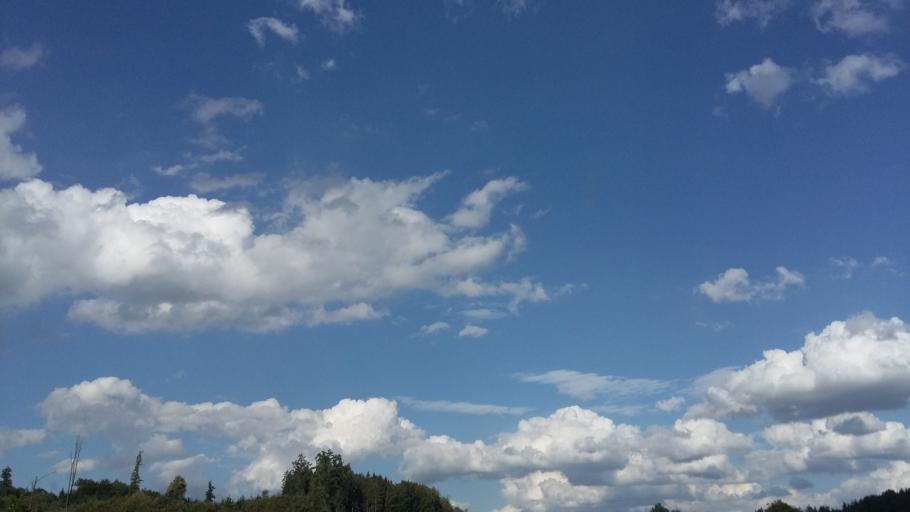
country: DE
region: Bavaria
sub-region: Swabia
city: Aystetten
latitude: 48.4199
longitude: 10.7847
